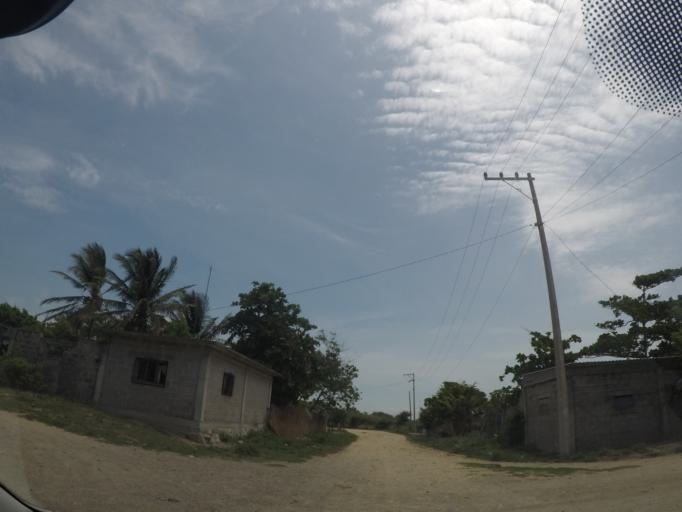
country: MX
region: Oaxaca
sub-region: San Mateo del Mar
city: Colonia Juarez
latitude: 16.2098
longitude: -95.0354
